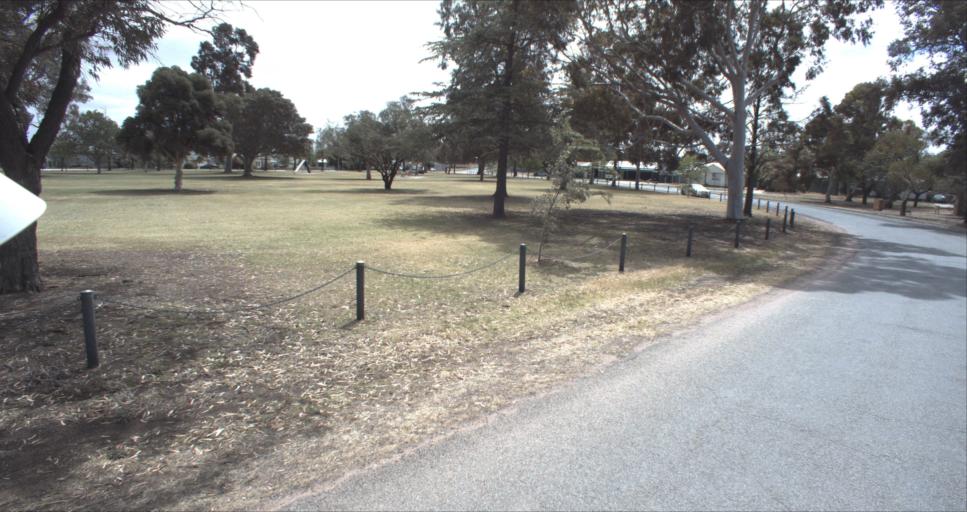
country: AU
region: New South Wales
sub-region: Leeton
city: Leeton
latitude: -34.5585
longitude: 146.3992
